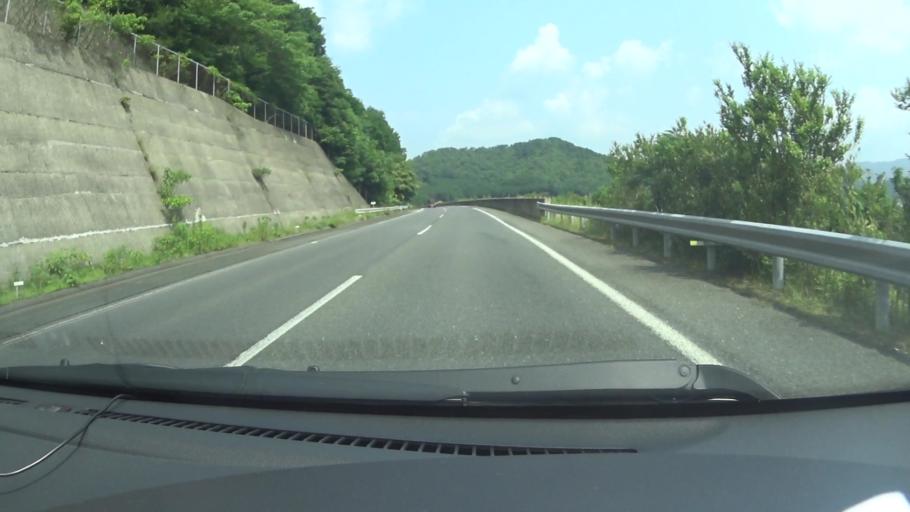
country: JP
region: Kyoto
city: Kameoka
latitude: 35.0632
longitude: 135.5288
